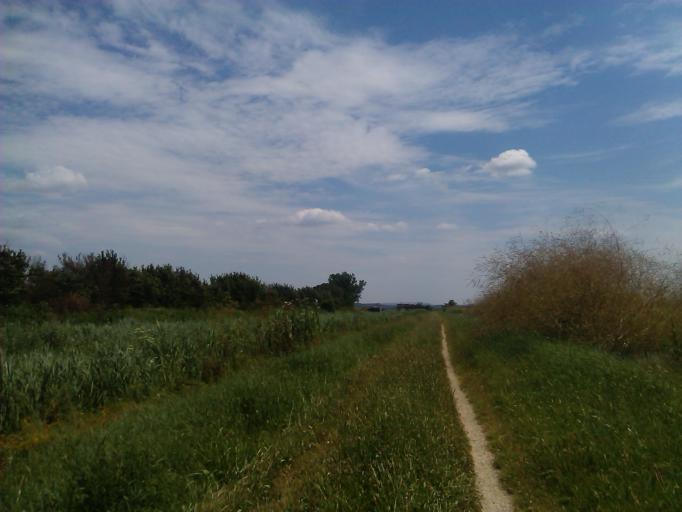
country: IT
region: Tuscany
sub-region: Provincia di Siena
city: Acquaviva
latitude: 43.1319
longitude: 11.9013
